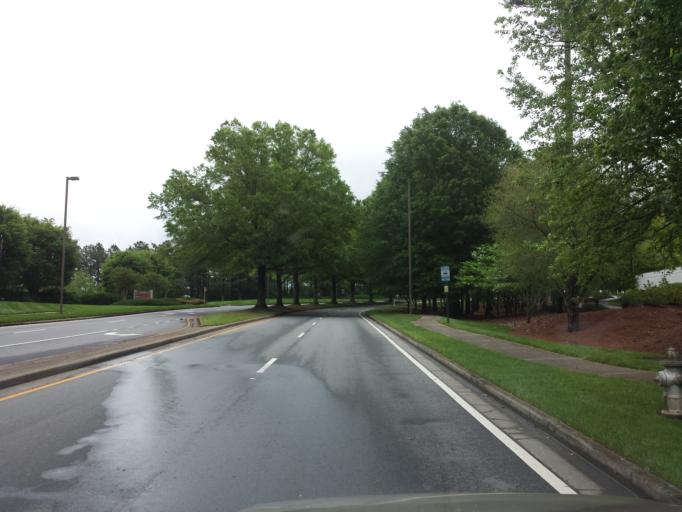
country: US
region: Georgia
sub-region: Cobb County
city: Kennesaw
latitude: 34.0042
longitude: -84.5861
